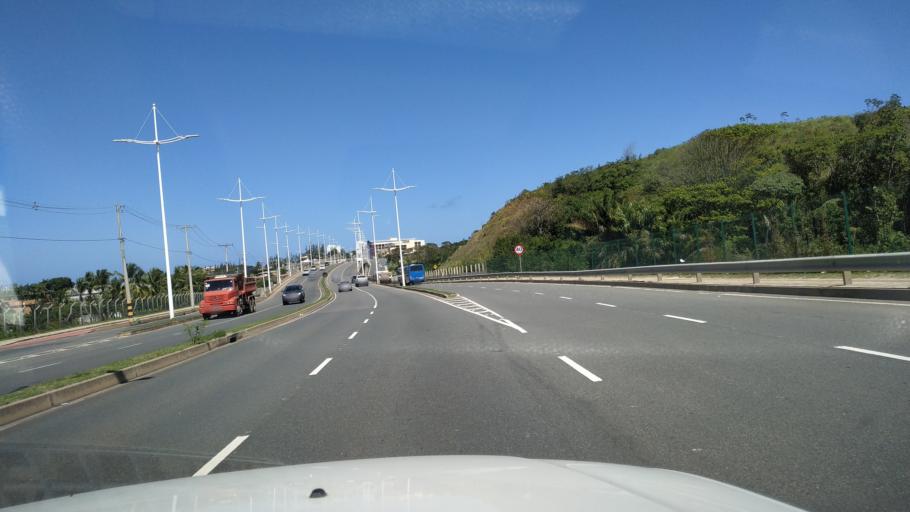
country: BR
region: Bahia
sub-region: Lauro De Freitas
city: Lauro de Freitas
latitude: -12.9345
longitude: -38.3848
